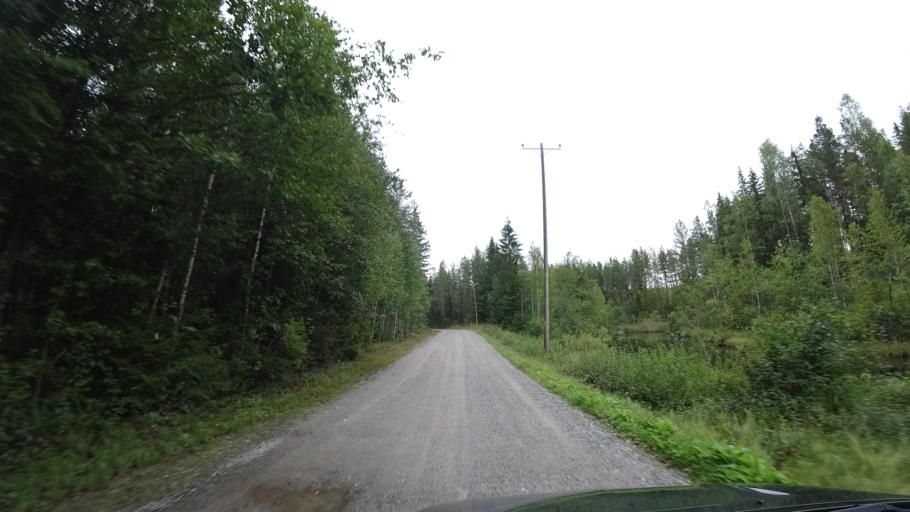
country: FI
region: Paijanne Tavastia
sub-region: Lahti
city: Auttoinen
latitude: 61.2174
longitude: 25.1366
